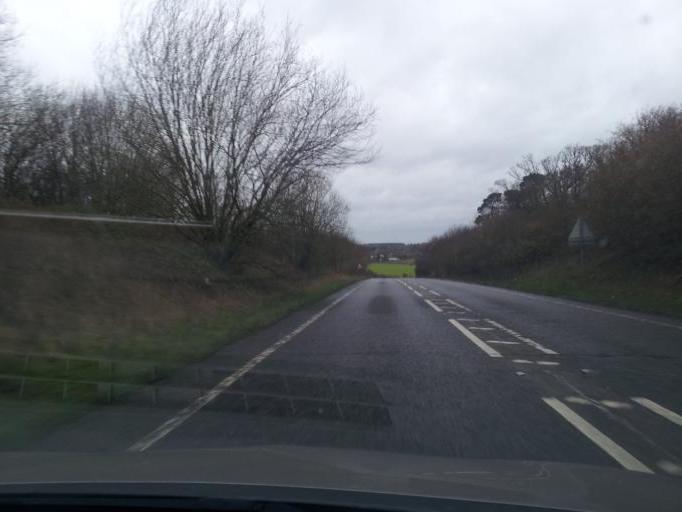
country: GB
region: England
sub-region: Suffolk
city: Botesdale
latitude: 52.3360
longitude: 0.9750
